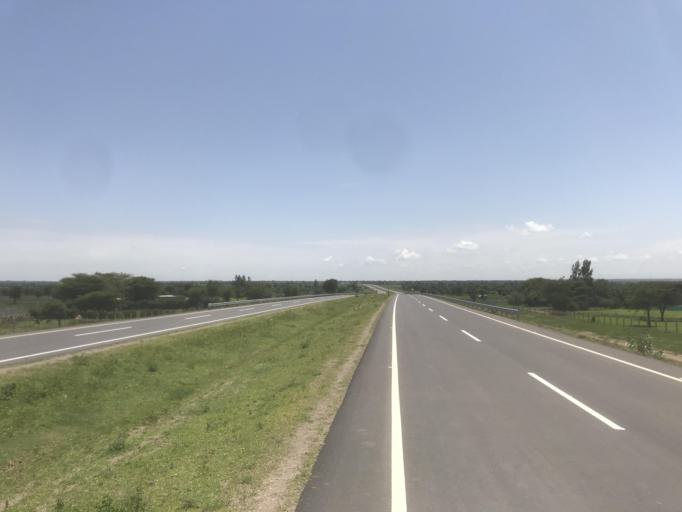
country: ET
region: Oromiya
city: Mojo
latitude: 8.3459
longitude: 38.9778
